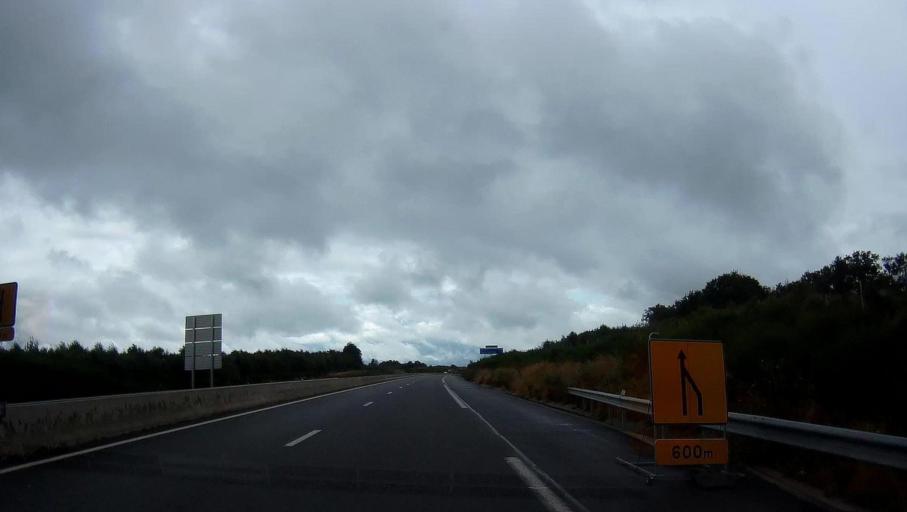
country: FR
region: Champagne-Ardenne
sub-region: Departement des Ardennes
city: Rocroi
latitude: 49.8946
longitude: 4.5208
